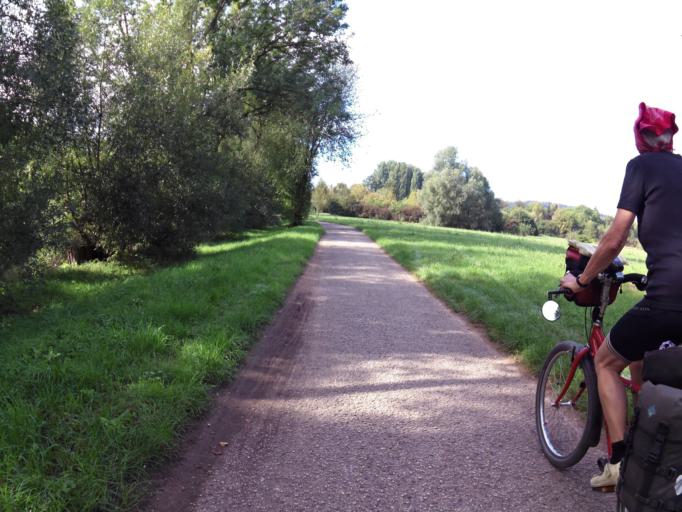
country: DE
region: Baden-Wuerttemberg
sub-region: Regierungsbezirk Stuttgart
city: Nurtingen
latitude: 48.6399
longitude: 9.3359
